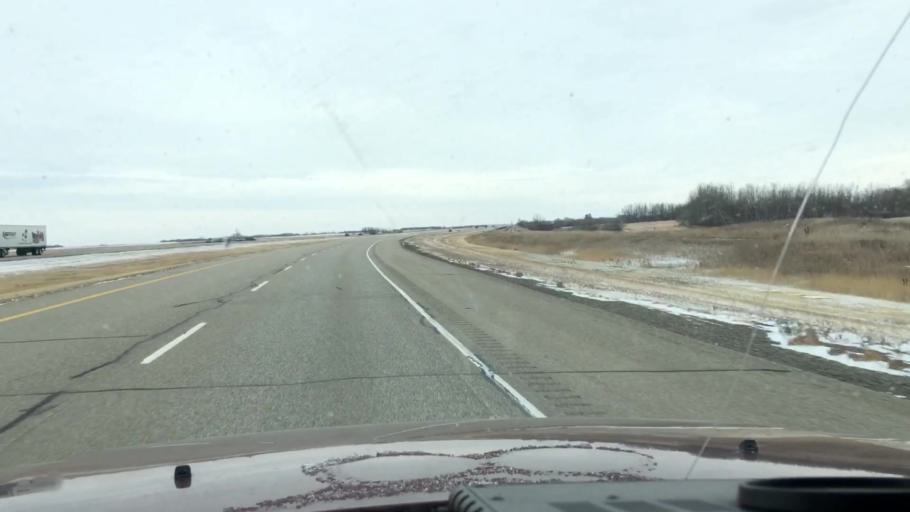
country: CA
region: Saskatchewan
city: Watrous
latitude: 51.3352
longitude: -106.0870
